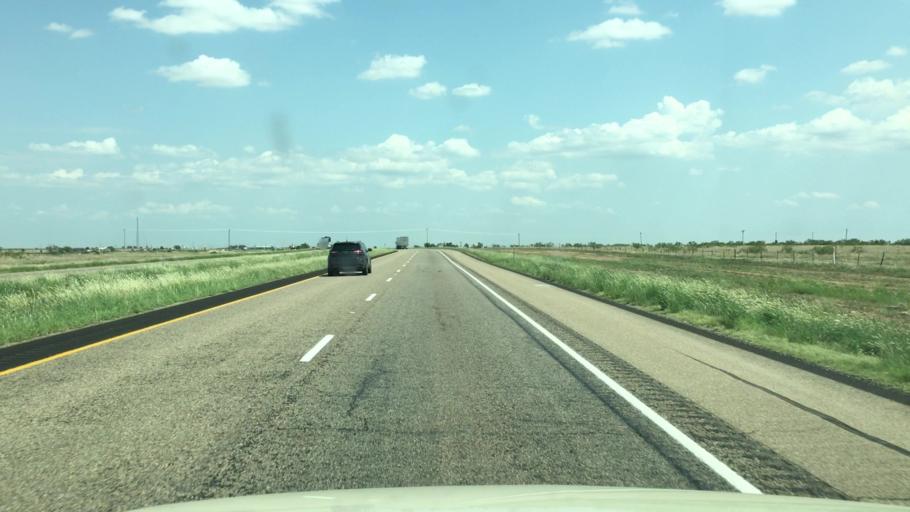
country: US
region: Texas
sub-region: Armstrong County
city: Claude
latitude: 35.0355
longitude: -101.1996
